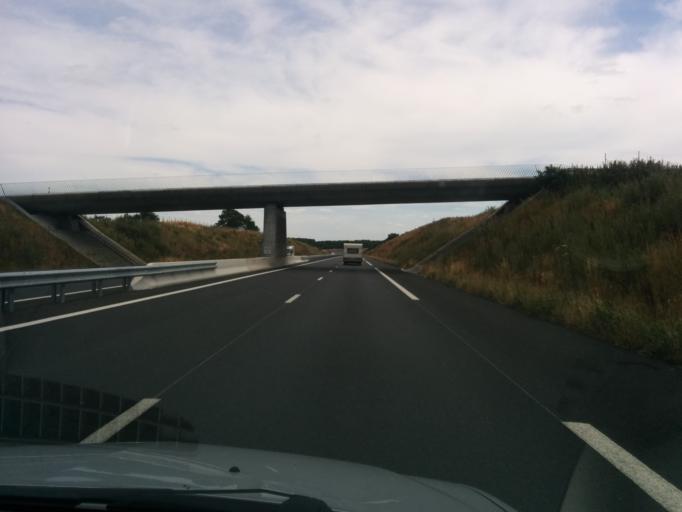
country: FR
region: Poitou-Charentes
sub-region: Departement des Deux-Sevres
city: Nueil-les-Aubiers
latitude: 46.8620
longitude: -0.5695
